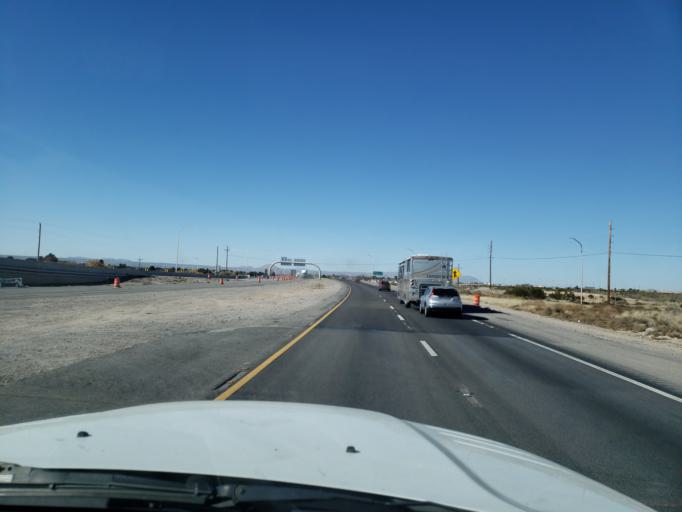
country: US
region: New Mexico
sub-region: Dona Ana County
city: University Park
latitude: 32.2635
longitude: -106.7350
